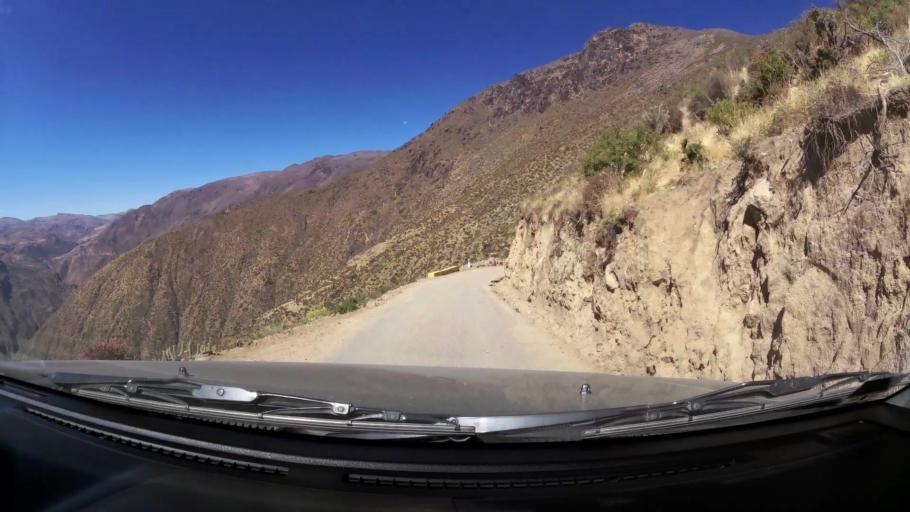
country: PE
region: Huancavelica
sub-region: Huaytara
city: Quito-Arma
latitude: -13.6197
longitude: -75.3523
